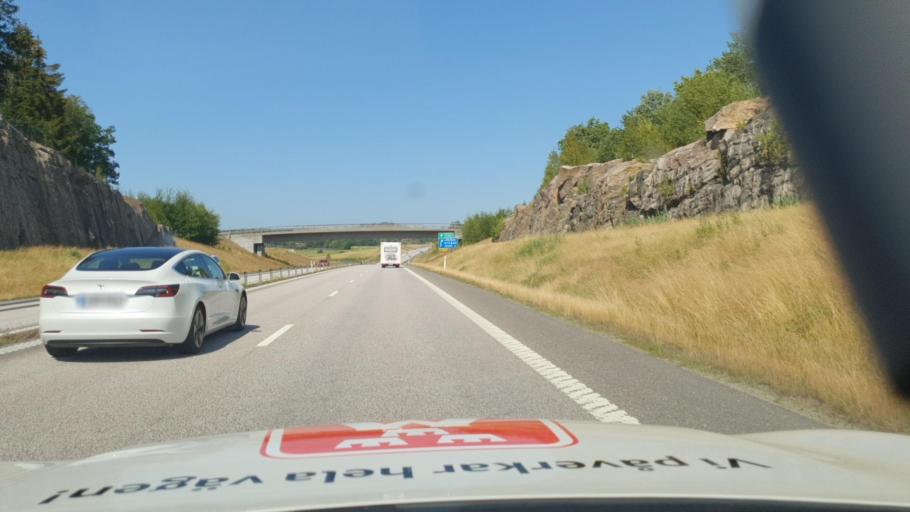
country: SE
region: Vaestra Goetaland
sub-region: Lilla Edets Kommun
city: Lodose
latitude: 58.0258
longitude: 12.1768
